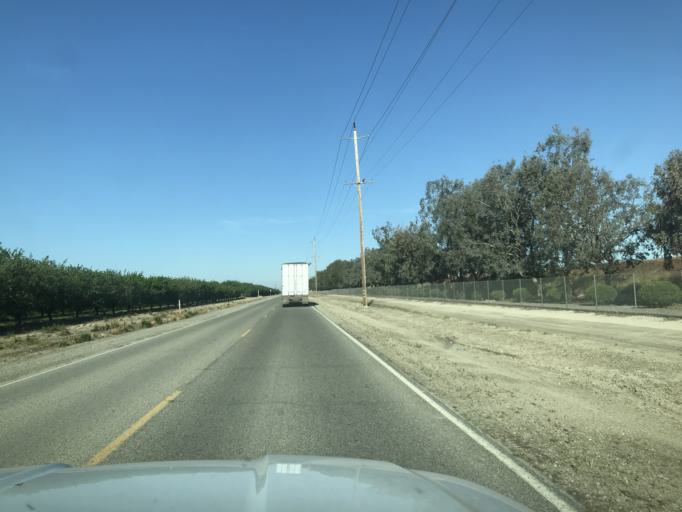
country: US
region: California
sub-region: Fresno County
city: San Joaquin
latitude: 36.6618
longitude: -120.1265
